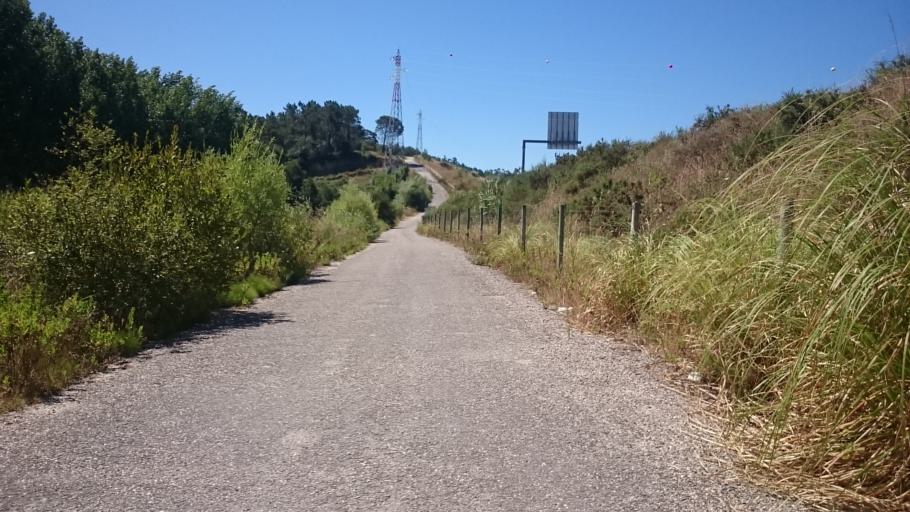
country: PT
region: Leiria
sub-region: Leiria
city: Souto da Carpalhosa
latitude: 39.8324
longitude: -8.8335
